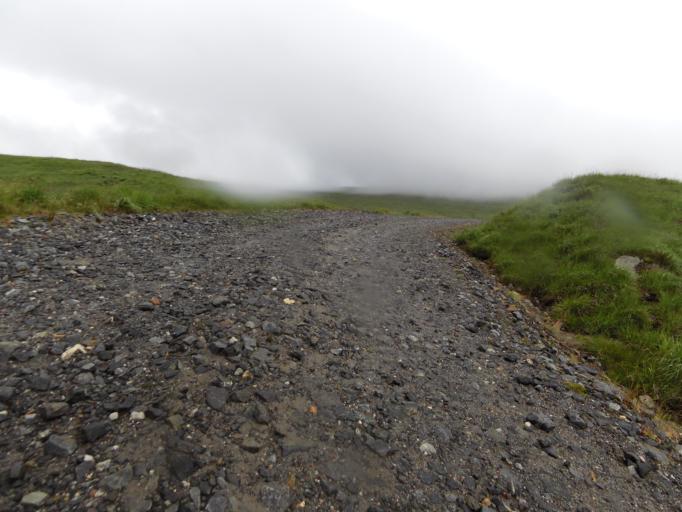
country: GB
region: Scotland
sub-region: Highland
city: Spean Bridge
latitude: 56.7683
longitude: -4.6735
